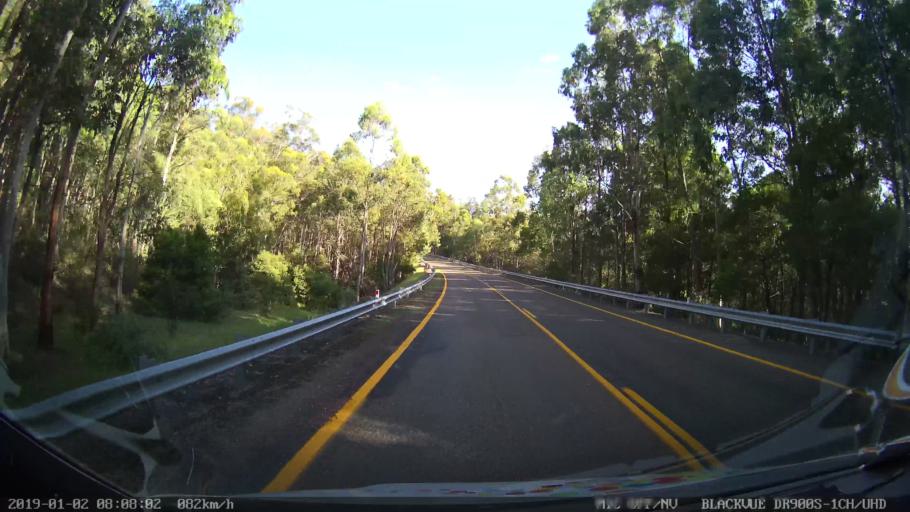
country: AU
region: New South Wales
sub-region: Tumut Shire
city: Tumut
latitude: -35.6203
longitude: 148.3885
